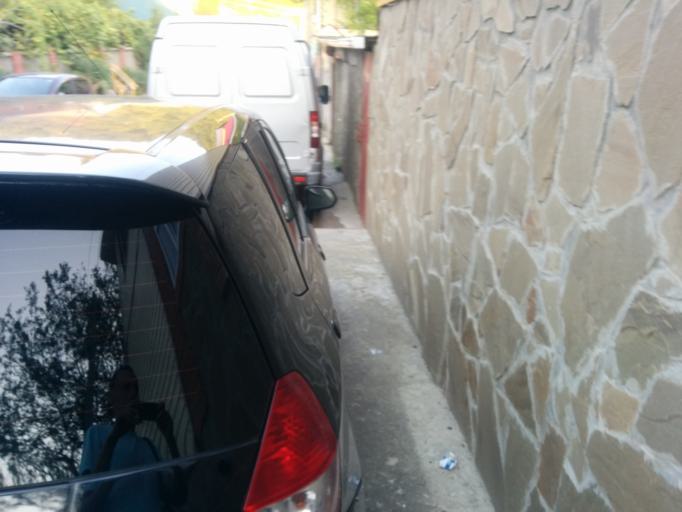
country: RU
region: Krasnodarskiy
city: Novomikhaylovskiy
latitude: 44.2609
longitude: 38.8222
